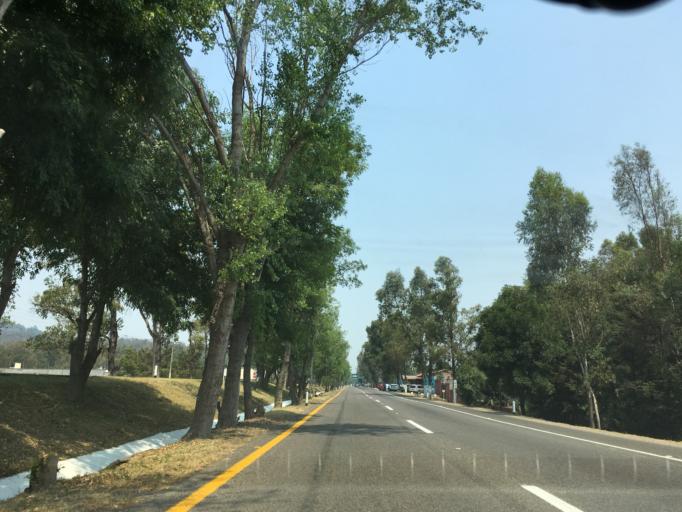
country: MX
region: Michoacan
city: Patzcuaro
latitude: 19.5406
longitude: -101.5796
